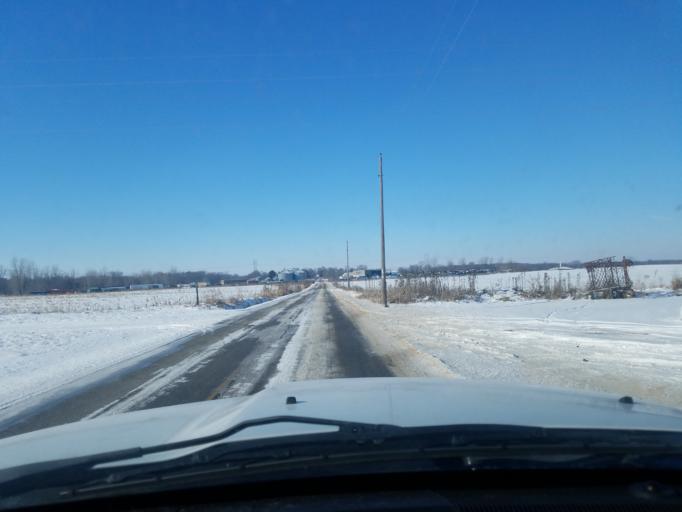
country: US
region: Indiana
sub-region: Noble County
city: Kendallville
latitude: 41.4113
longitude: -85.2507
